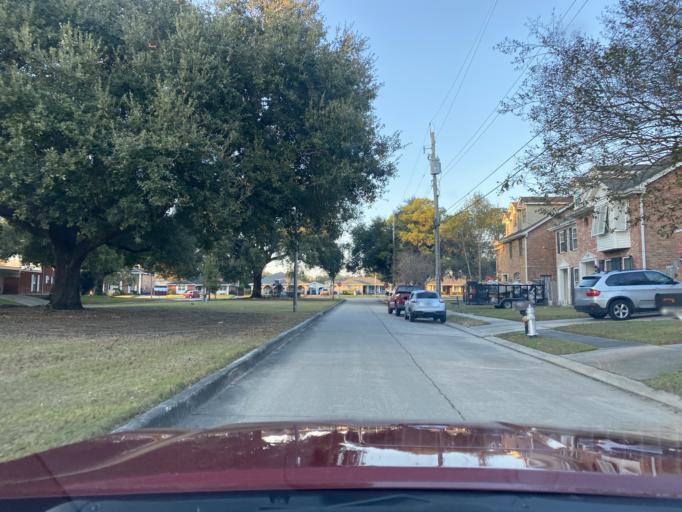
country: US
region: Louisiana
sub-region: Orleans Parish
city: New Orleans
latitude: 30.0247
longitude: -90.0565
